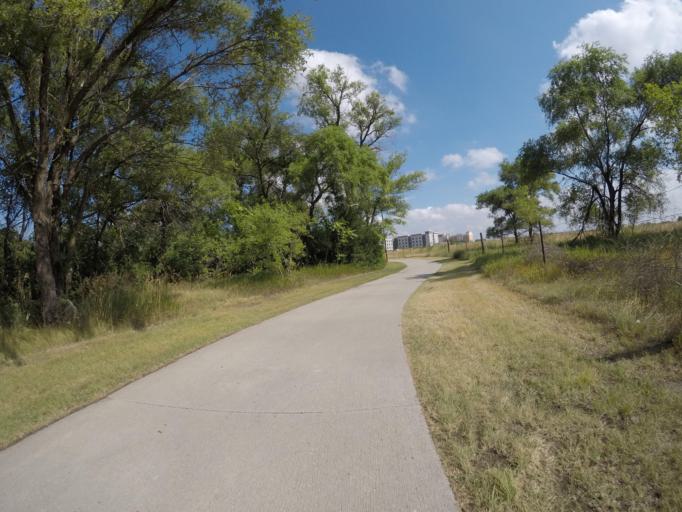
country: US
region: Nebraska
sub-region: Buffalo County
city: Kearney
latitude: 40.6765
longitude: -99.0918
